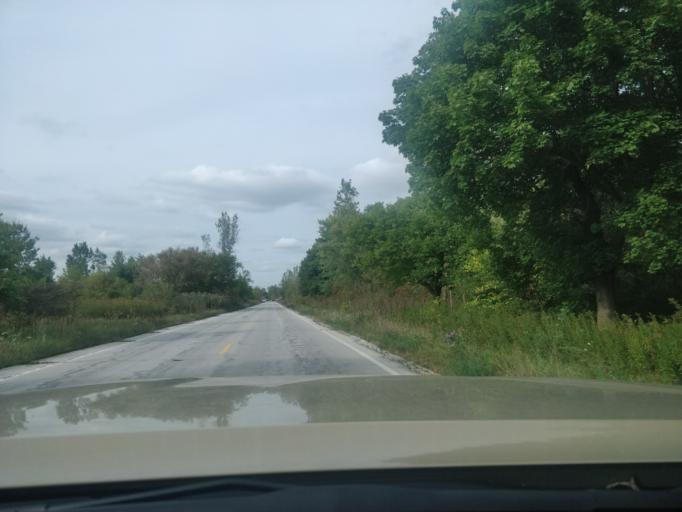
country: US
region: Michigan
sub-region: Wayne County
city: Romulus
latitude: 42.1751
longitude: -83.3644
